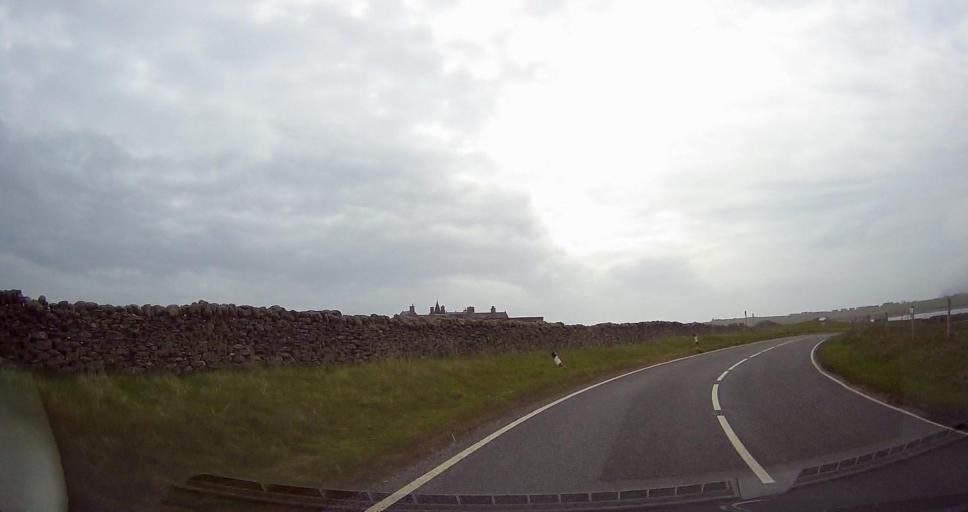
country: GB
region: Scotland
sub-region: Shetland Islands
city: Sandwick
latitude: 59.8703
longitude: -1.2834
